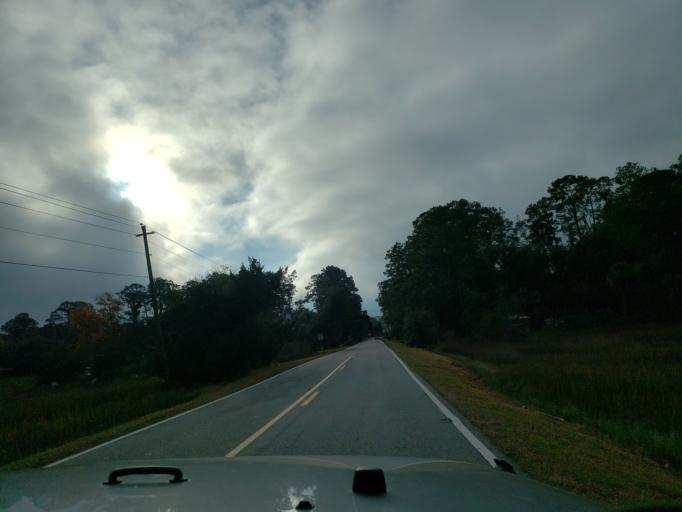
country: US
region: Georgia
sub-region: Chatham County
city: Wilmington Island
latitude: 32.0169
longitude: -80.9616
